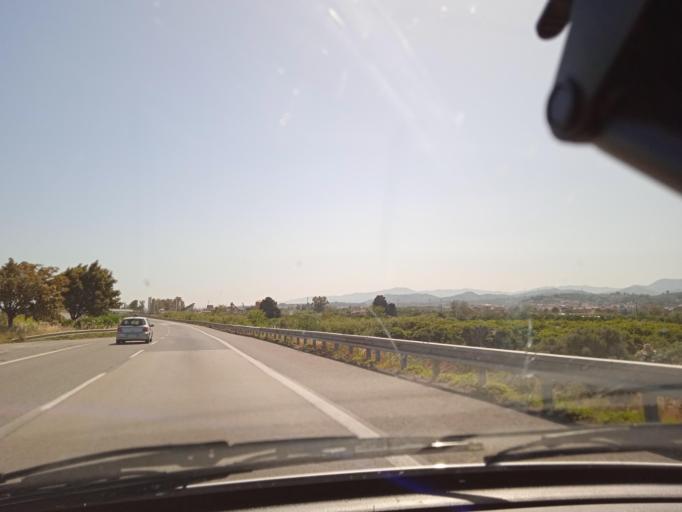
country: IT
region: Sicily
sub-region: Messina
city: Meri
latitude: 38.1713
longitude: 15.2303
